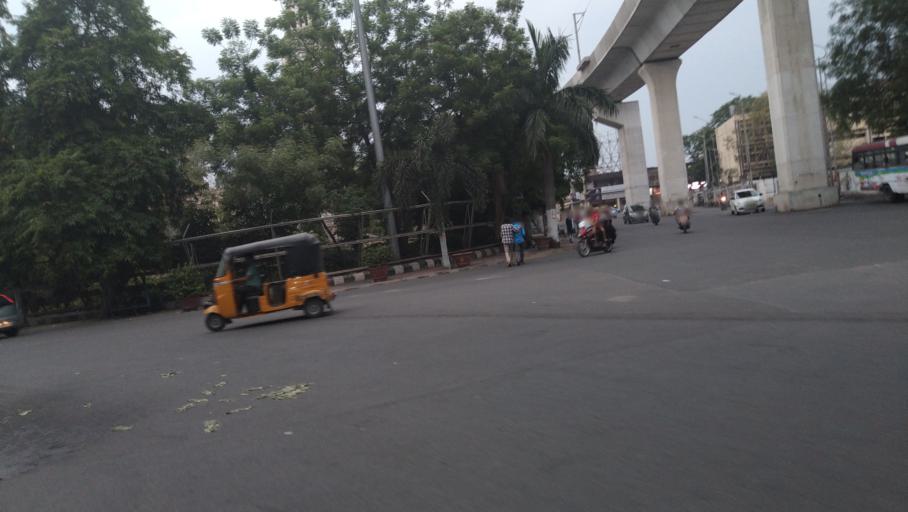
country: IN
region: Telangana
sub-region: Hyderabad
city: Malkajgiri
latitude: 17.4403
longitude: 78.4987
